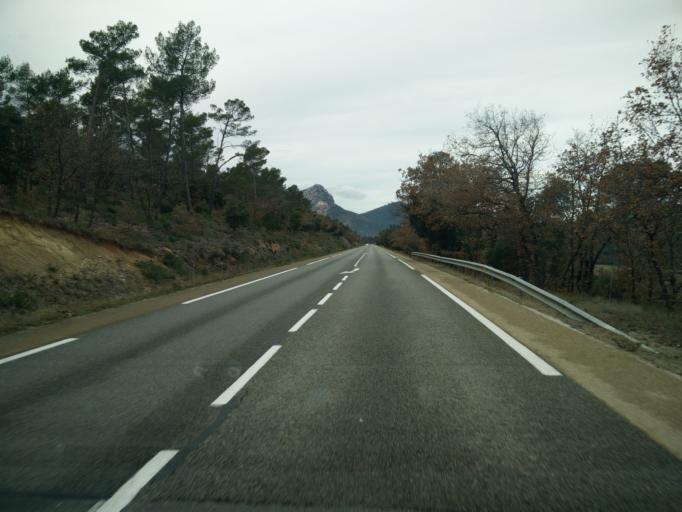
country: FR
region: Provence-Alpes-Cote d'Azur
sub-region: Departement du Var
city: Camps-la-Source
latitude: 43.3783
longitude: 6.0812
